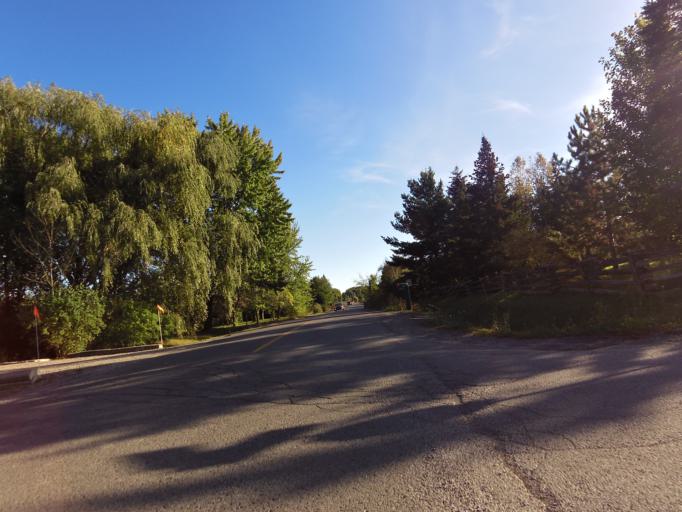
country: CA
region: Ontario
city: Bells Corners
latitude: 45.4558
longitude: -75.8837
